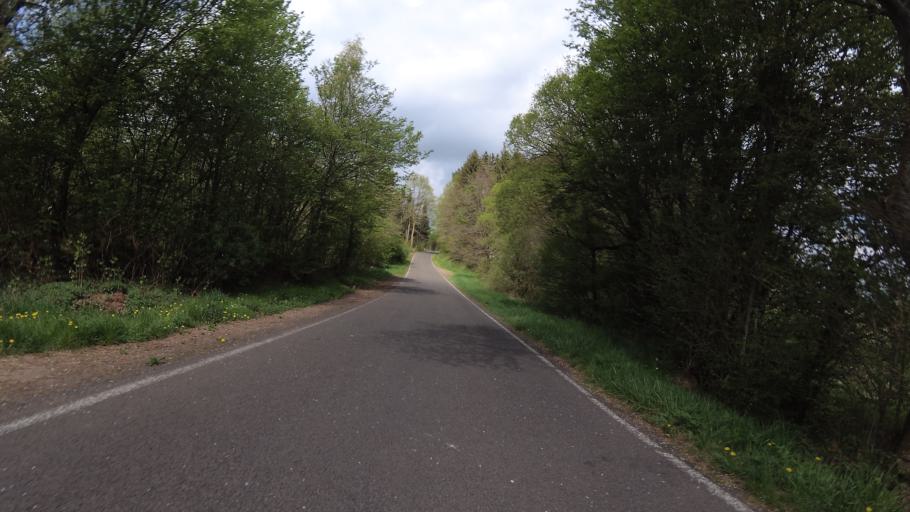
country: DE
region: Saarland
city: Wadern
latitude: 49.5524
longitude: 6.8879
